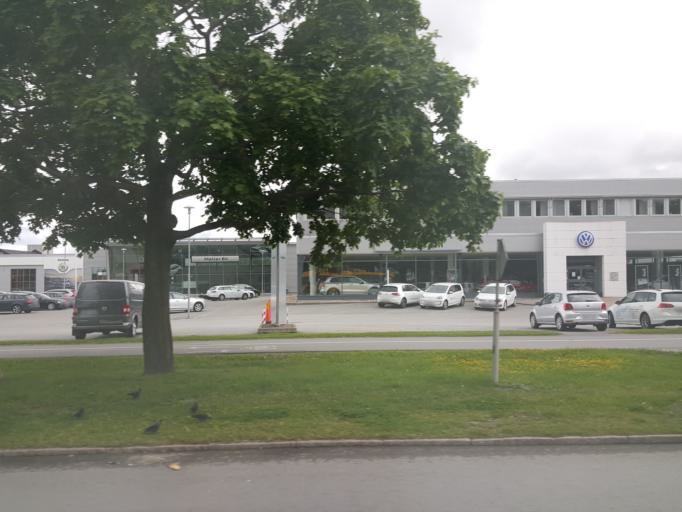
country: SE
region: Uppsala
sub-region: Uppsala Kommun
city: Uppsala
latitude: 59.8478
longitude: 17.6631
